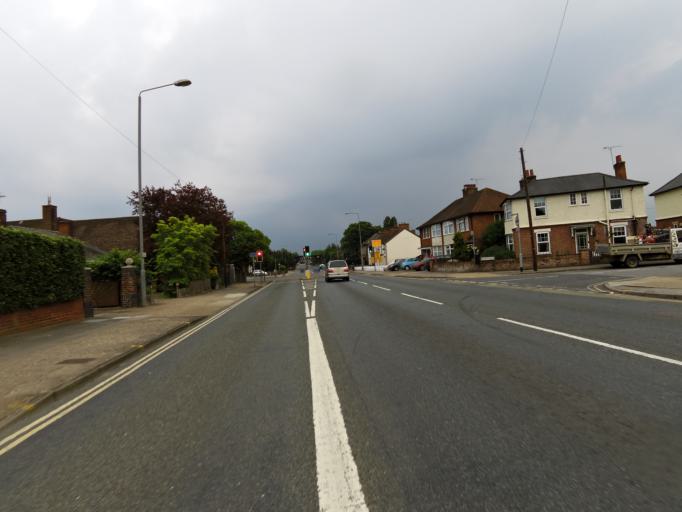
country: GB
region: England
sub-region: Suffolk
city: Ipswich
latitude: 52.0729
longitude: 1.1318
